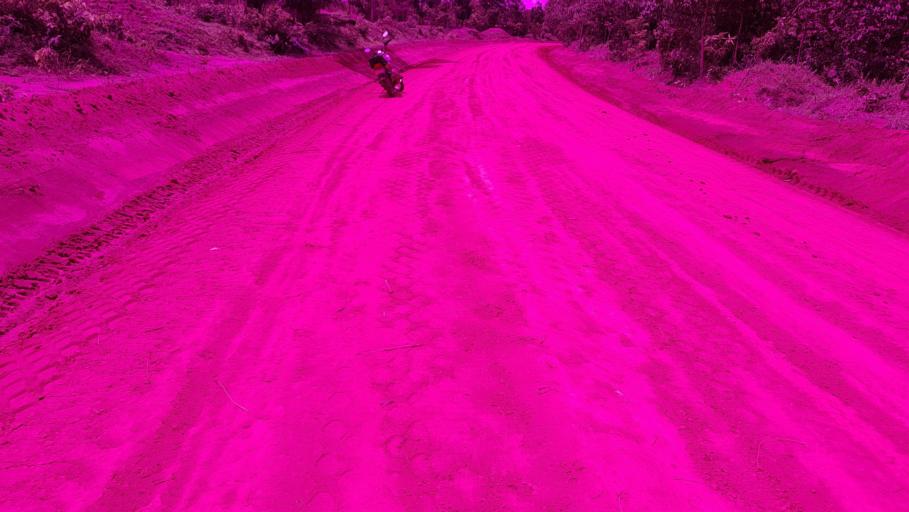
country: GN
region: Boke
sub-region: Boffa
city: Boffa
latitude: 10.0524
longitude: -13.8736
